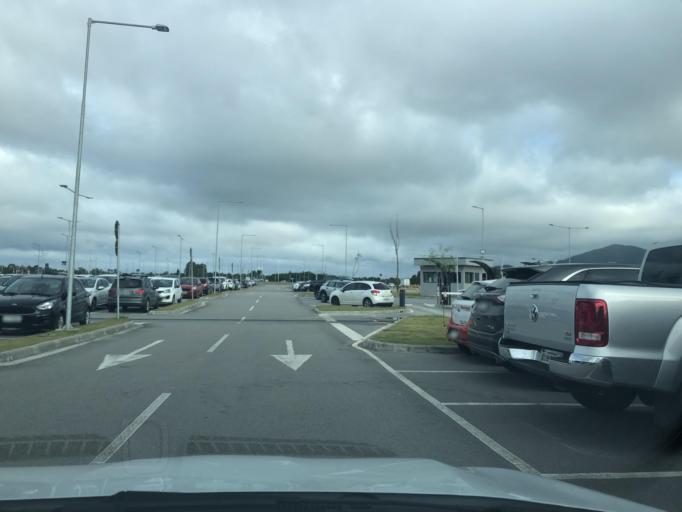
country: BR
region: Santa Catarina
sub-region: Florianopolis
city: Tapera
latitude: -27.6754
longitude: -48.5465
